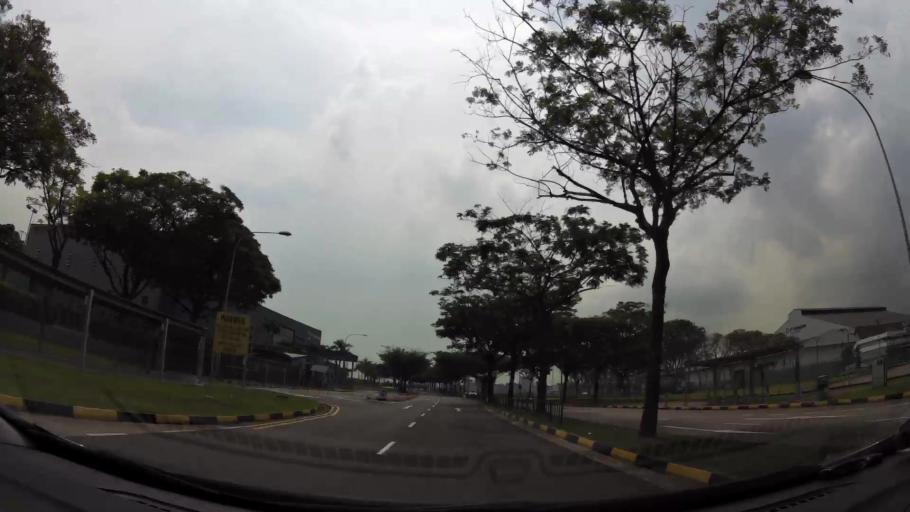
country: SG
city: Singapore
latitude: 1.3505
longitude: 103.8990
